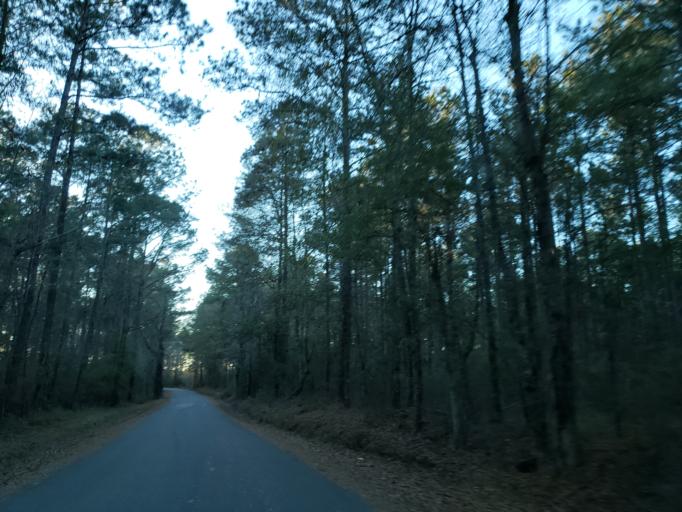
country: US
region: Mississippi
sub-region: Covington County
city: Collins
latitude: 31.5706
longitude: -89.4396
